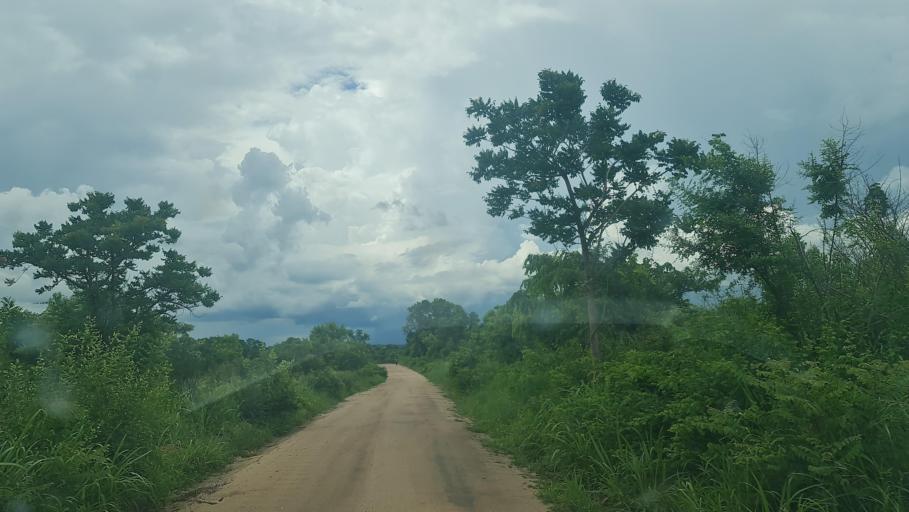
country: MW
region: Southern Region
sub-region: Nsanje District
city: Nsanje
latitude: -17.5930
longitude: 35.6746
